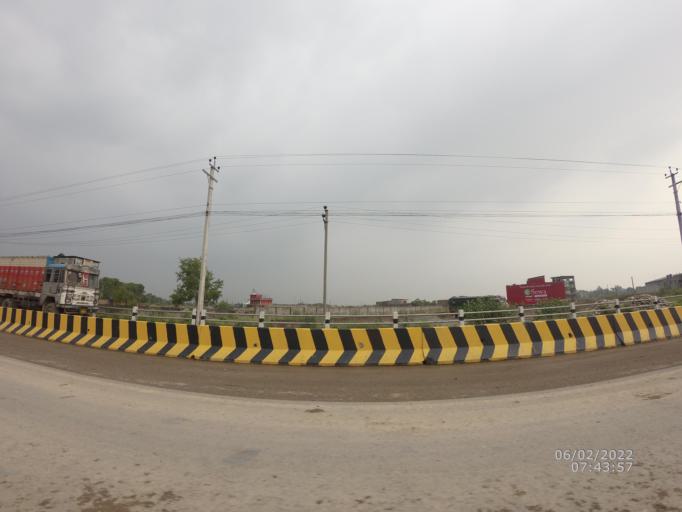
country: NP
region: Western Region
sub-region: Lumbini Zone
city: Bhairahawa
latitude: 27.5149
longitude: 83.4329
